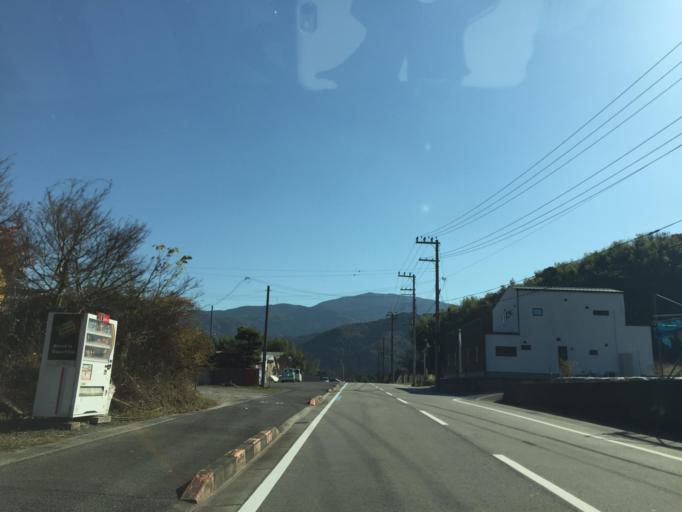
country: JP
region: Wakayama
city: Iwade
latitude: 34.1518
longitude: 135.3447
